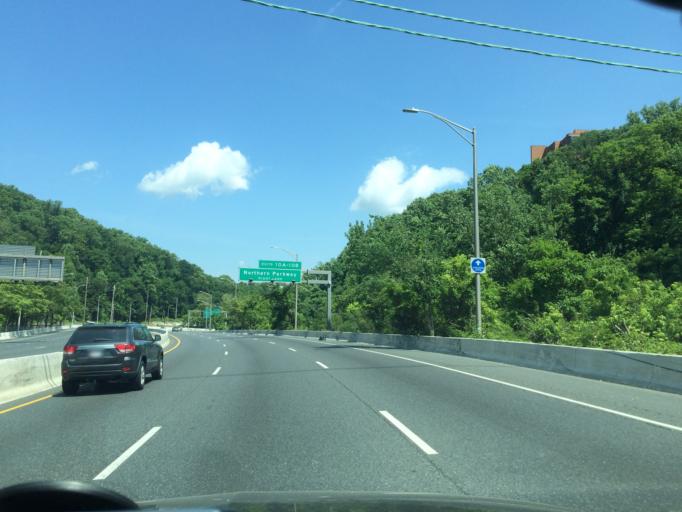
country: US
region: Maryland
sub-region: Baltimore County
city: Towson
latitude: 39.3540
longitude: -76.6478
